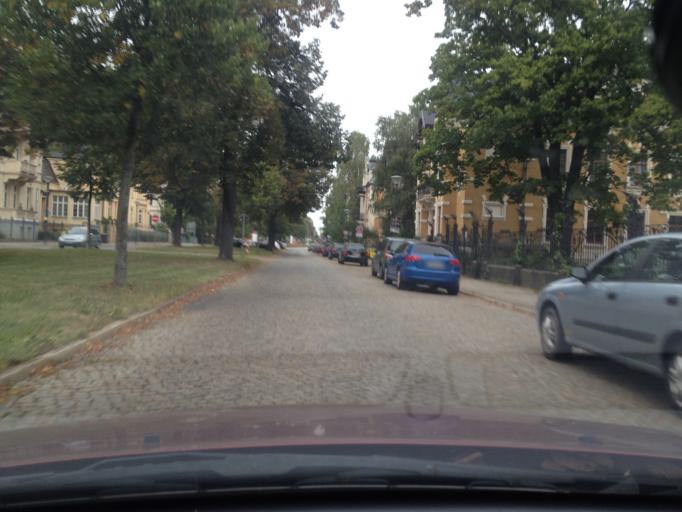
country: DE
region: Saxony
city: Goerlitz
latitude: 51.1416
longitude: 14.9864
